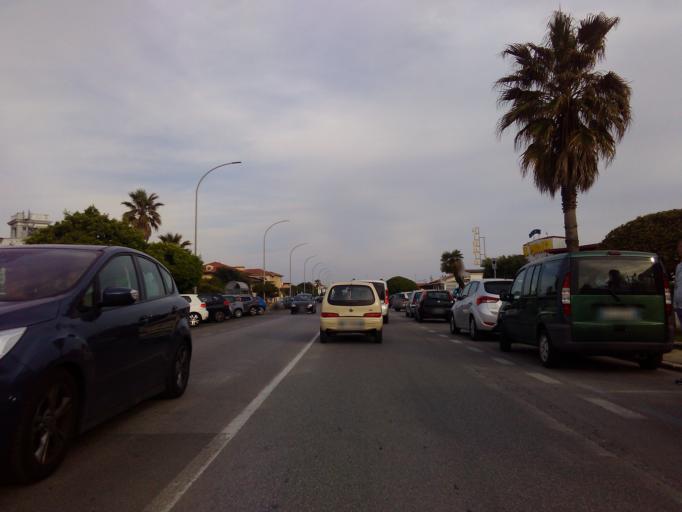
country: IT
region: Tuscany
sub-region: Provincia di Massa-Carrara
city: Massa
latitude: 44.0062
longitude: 10.1016
